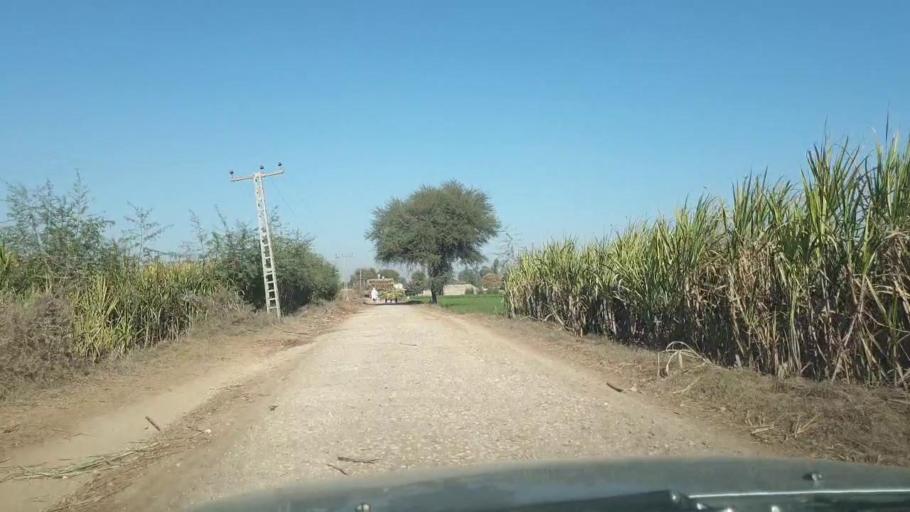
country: PK
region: Sindh
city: Ghotki
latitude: 28.0939
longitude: 69.3430
